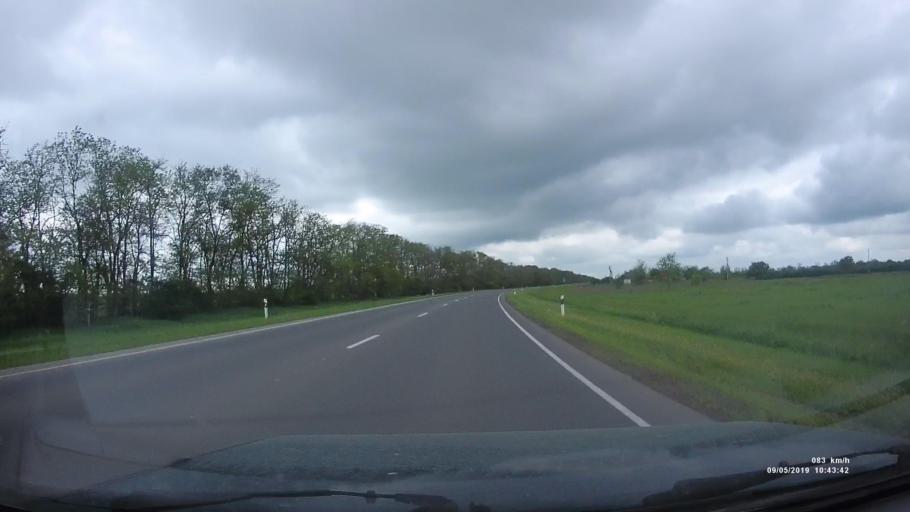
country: RU
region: Rostov
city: Peshkovo
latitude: 47.0054
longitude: 39.4008
